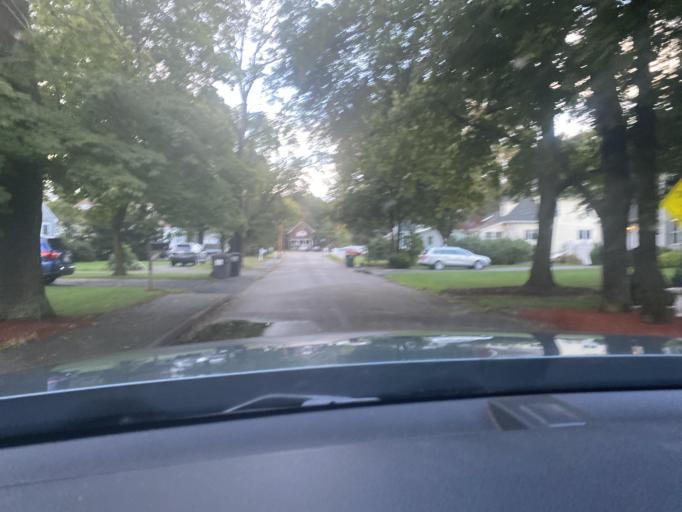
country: US
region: Massachusetts
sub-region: Norfolk County
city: Millis-Clicquot
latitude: 42.1707
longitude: -71.3500
